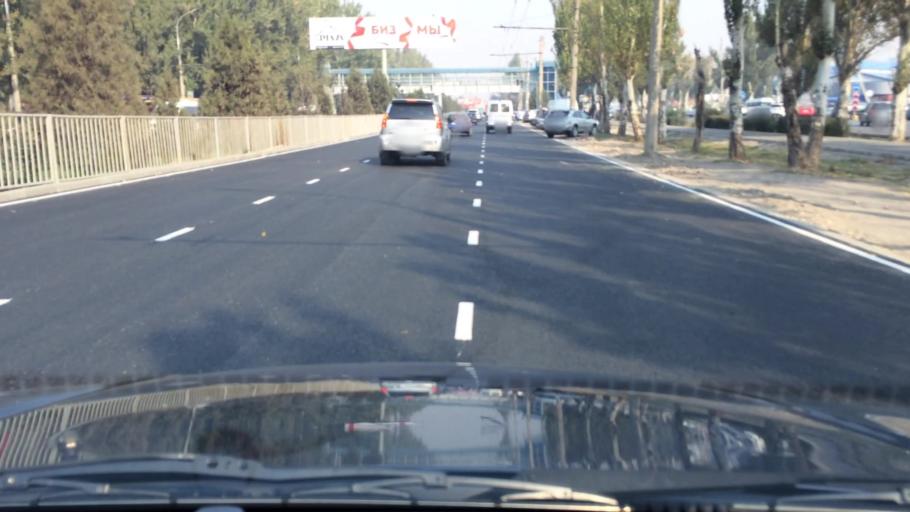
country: KG
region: Chuy
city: Lebedinovka
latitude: 42.8701
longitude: 74.6368
